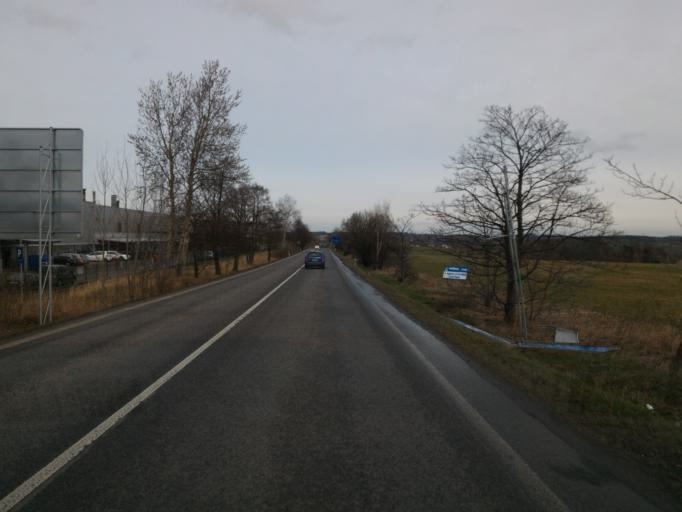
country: CZ
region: Ustecky
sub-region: Okres Decin
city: Rumburk
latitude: 50.9335
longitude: 14.5585
